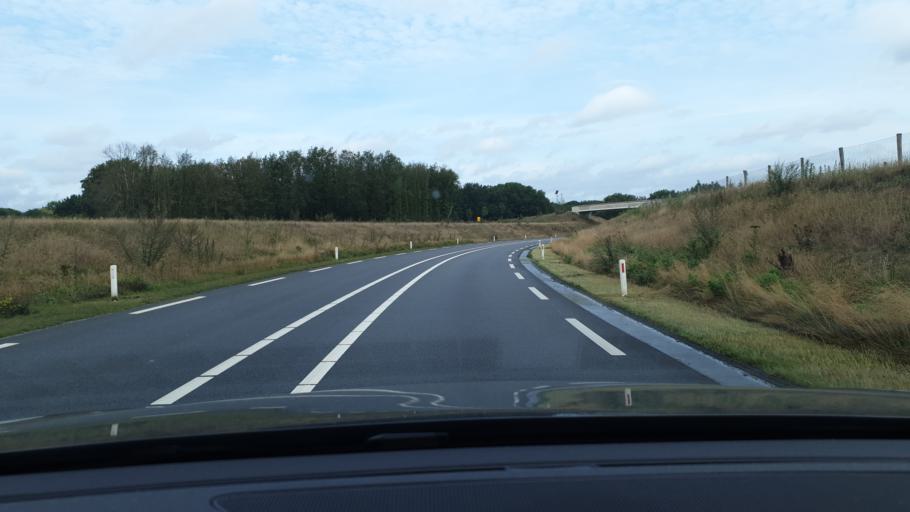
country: NL
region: Limburg
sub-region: Gemeente Bergen
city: Wellerlooi
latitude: 51.5357
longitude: 6.0642
